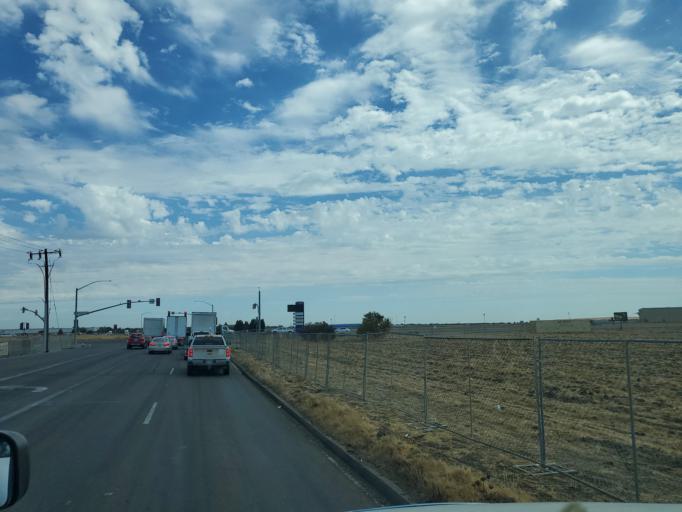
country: US
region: California
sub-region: San Joaquin County
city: French Camp
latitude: 37.9016
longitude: -121.2561
